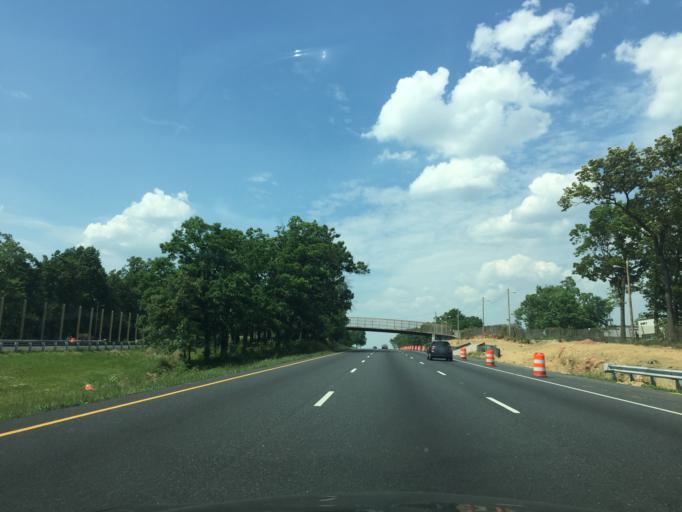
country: US
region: Maryland
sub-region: Baltimore County
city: Baltimore Highlands
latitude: 39.2369
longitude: -76.6490
